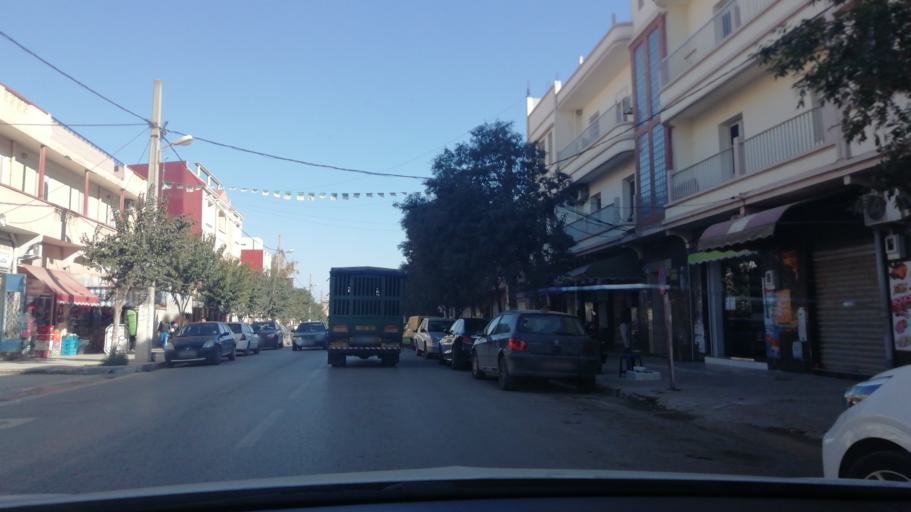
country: DZ
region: Tlemcen
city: Nedroma
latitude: 35.0435
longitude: -1.8862
